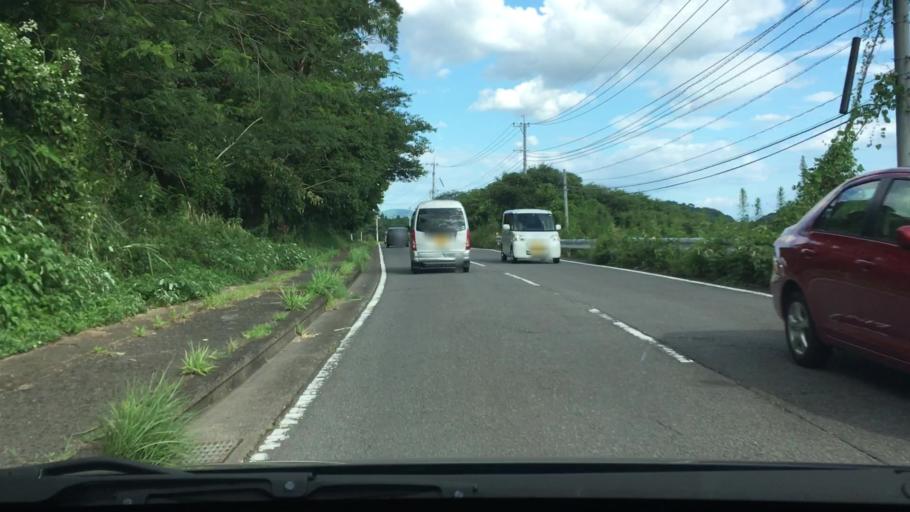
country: JP
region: Nagasaki
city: Togitsu
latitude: 32.8199
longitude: 129.7361
